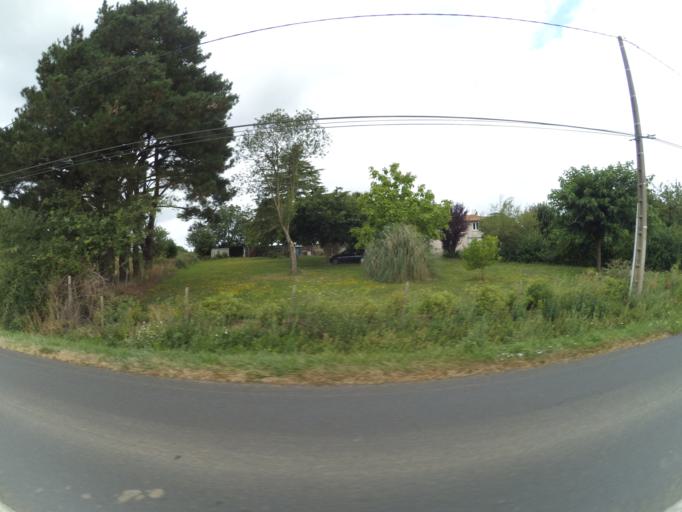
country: FR
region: Pays de la Loire
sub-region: Departement de Maine-et-Loire
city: Montfaucon-Montigne
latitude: 47.1075
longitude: -1.1136
